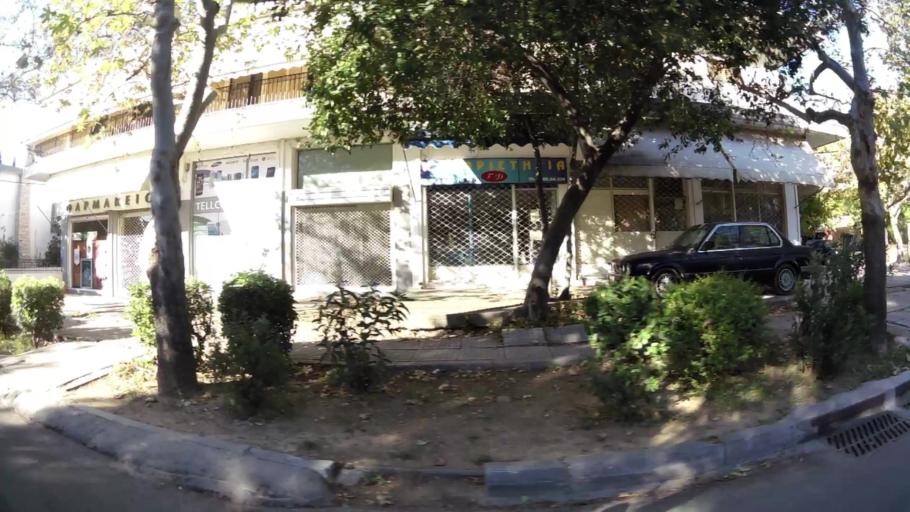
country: GR
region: Attica
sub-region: Nomarchia Athinas
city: Kifisia
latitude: 38.0756
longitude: 23.8038
